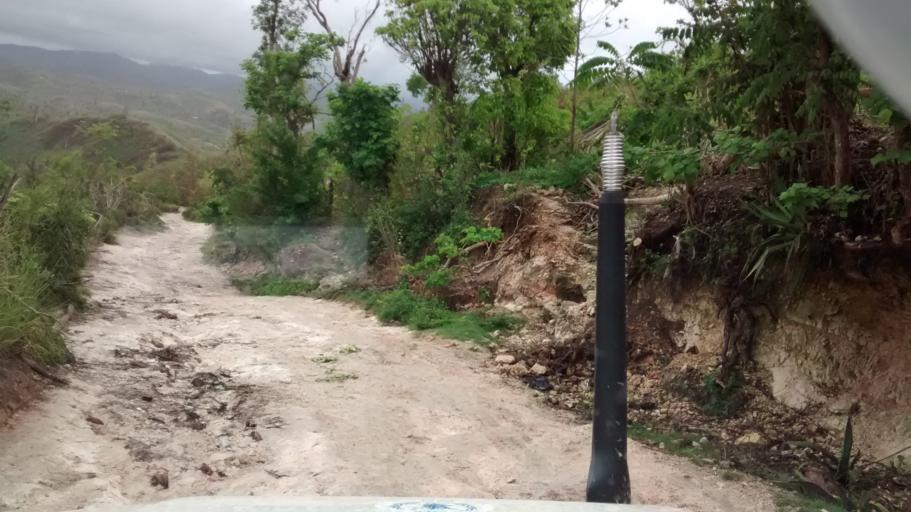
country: HT
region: Grandans
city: Jeremie
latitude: 18.5815
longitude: -74.1495
